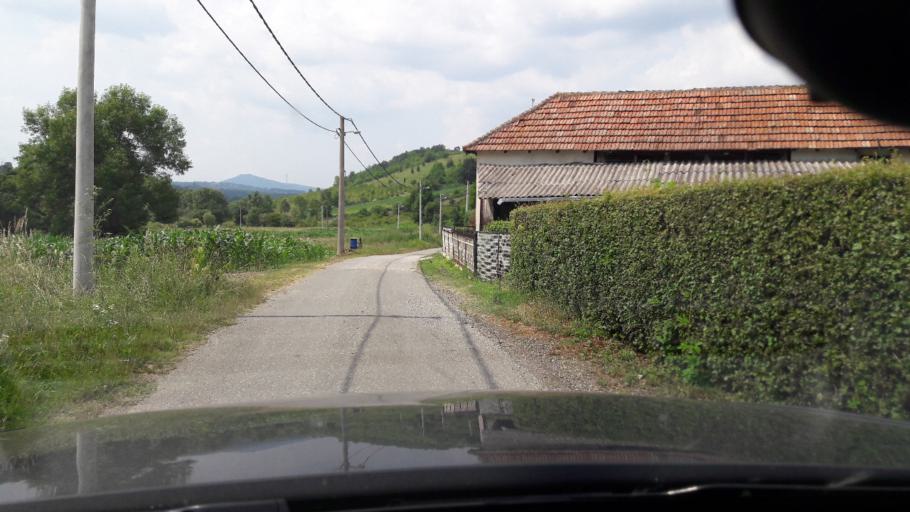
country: RS
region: Central Serbia
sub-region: Belgrade
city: Sopot
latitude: 44.6333
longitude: 20.5928
